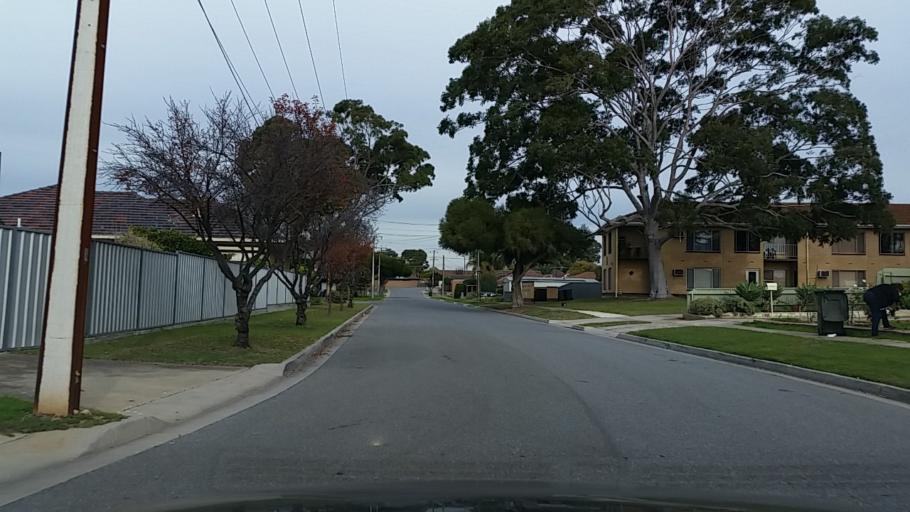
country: AU
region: South Australia
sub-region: Charles Sturt
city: Seaton
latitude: -34.9045
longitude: 138.5183
